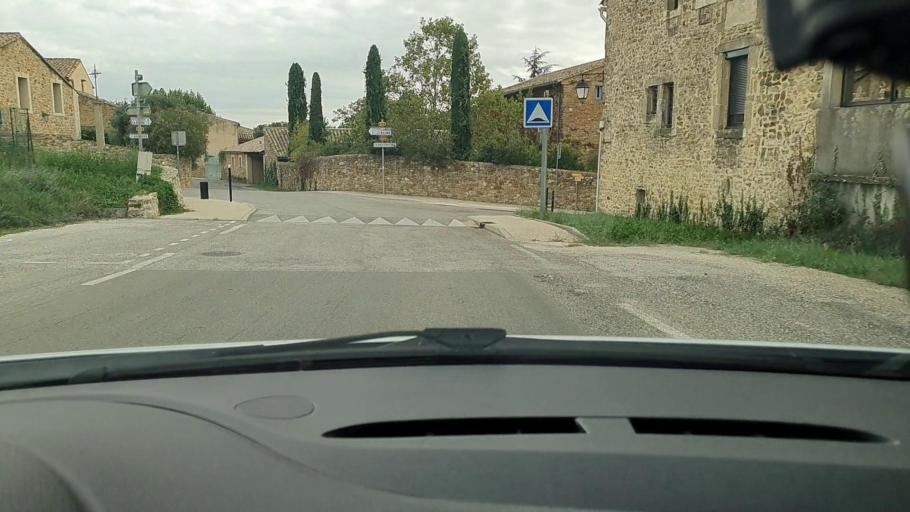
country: FR
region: Languedoc-Roussillon
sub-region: Departement du Gard
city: Montaren-et-Saint-Mediers
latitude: 44.0497
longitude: 4.3220
